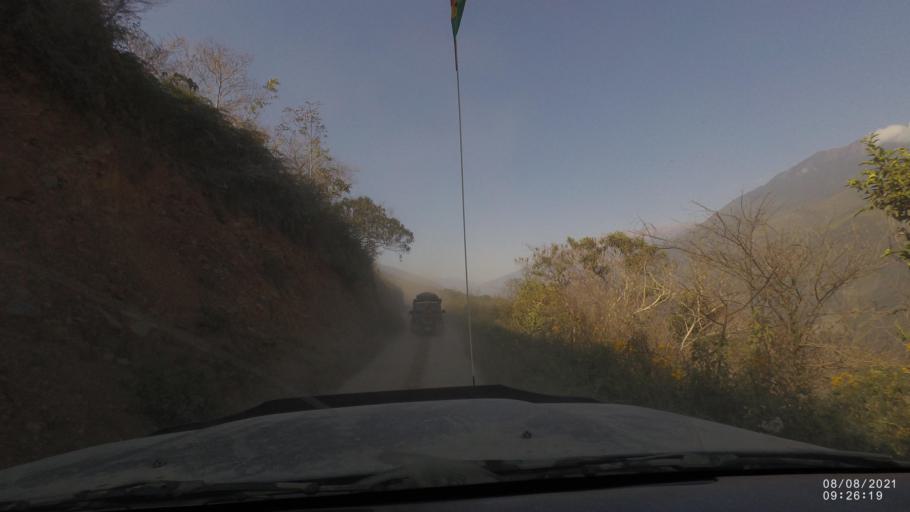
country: BO
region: La Paz
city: Quime
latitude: -16.5866
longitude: -66.7210
